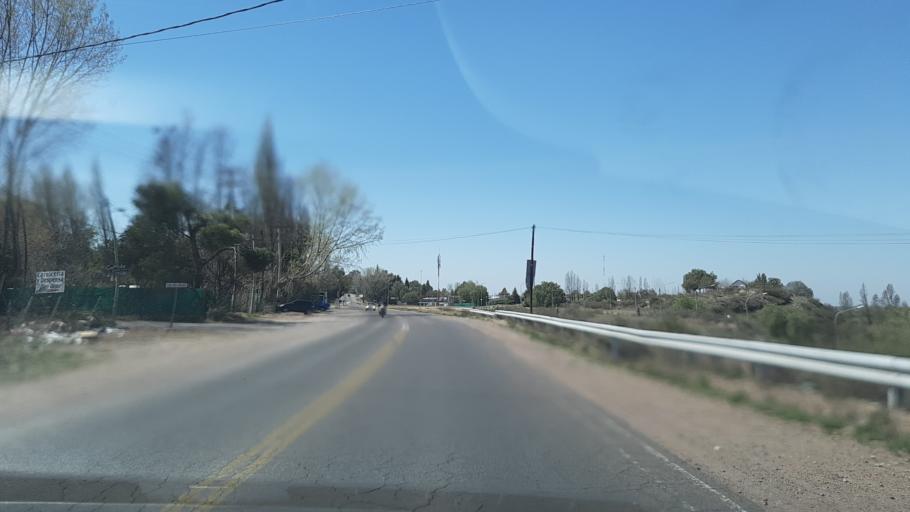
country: AR
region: Mendoza
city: Lujan de Cuyo
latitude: -33.0168
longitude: -68.9345
